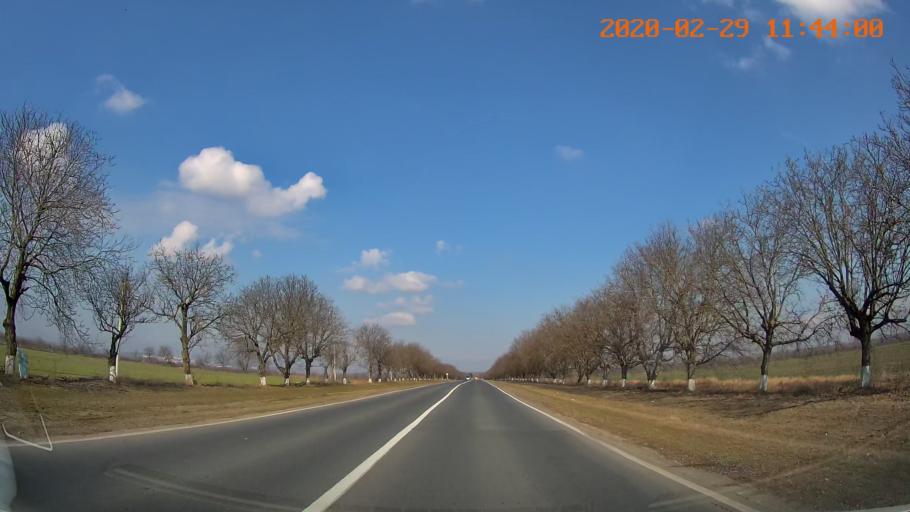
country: MD
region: Rezina
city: Saharna
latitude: 47.7046
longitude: 29.0011
